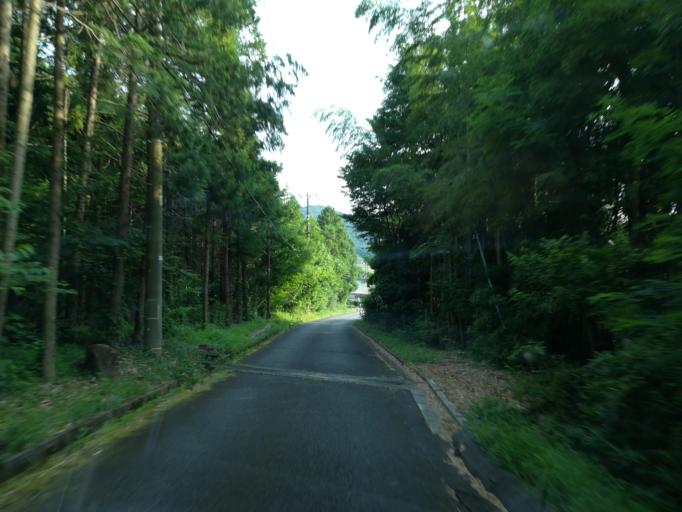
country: JP
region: Ibaraki
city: Tsukuba
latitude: 36.2014
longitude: 140.1083
